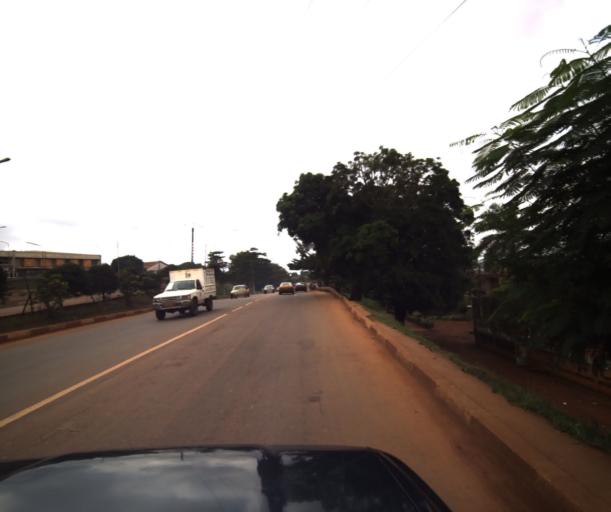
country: CM
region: Centre
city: Yaounde
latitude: 3.8342
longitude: 11.5190
